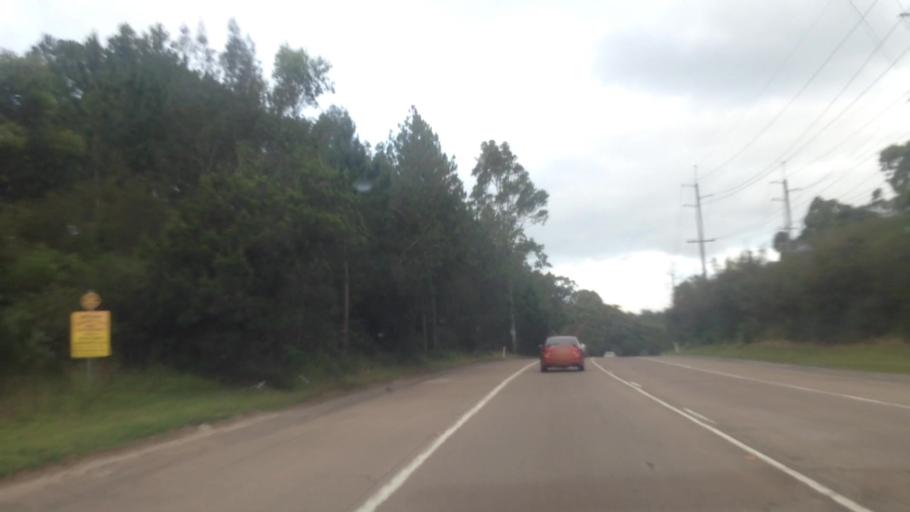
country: AU
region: New South Wales
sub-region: Lake Macquarie Shire
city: Dora Creek
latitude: -33.1154
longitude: 151.4713
